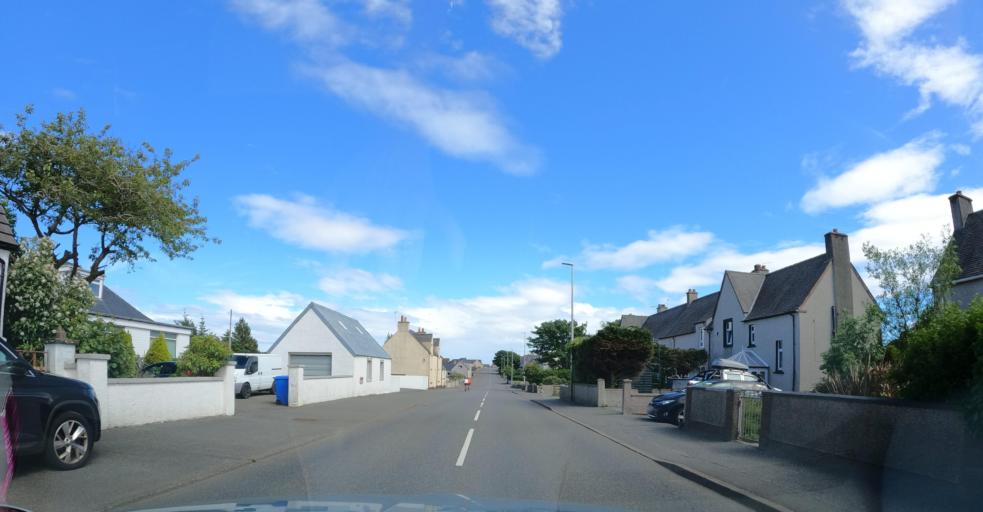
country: GB
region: Scotland
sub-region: Eilean Siar
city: Isle of Lewis
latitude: 58.2191
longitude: -6.3836
